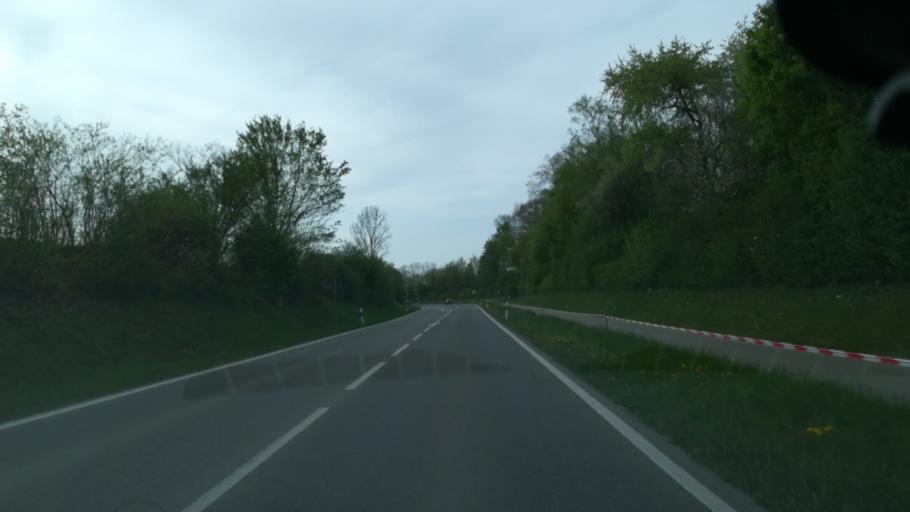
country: DE
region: Baden-Wuerttemberg
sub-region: Freiburg Region
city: Moos
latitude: 47.7545
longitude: 8.9149
